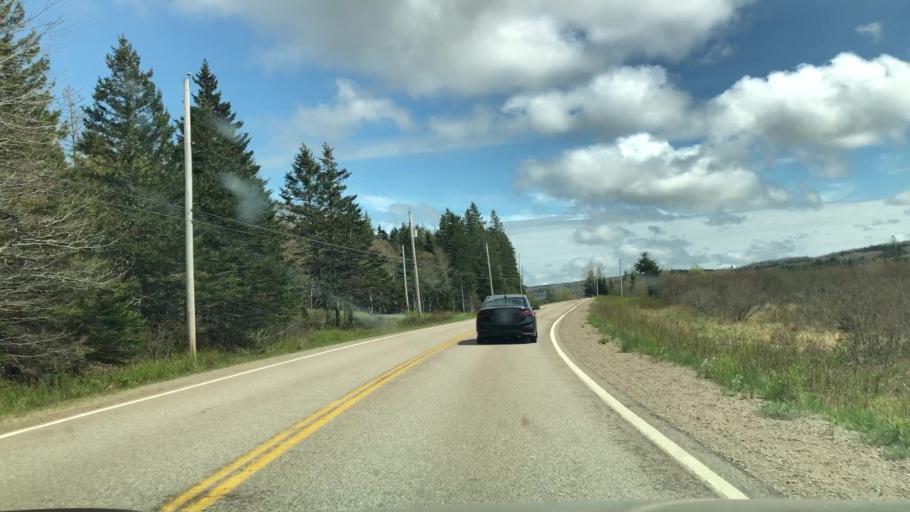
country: CA
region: Nova Scotia
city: Antigonish
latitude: 45.1903
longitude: -61.9896
